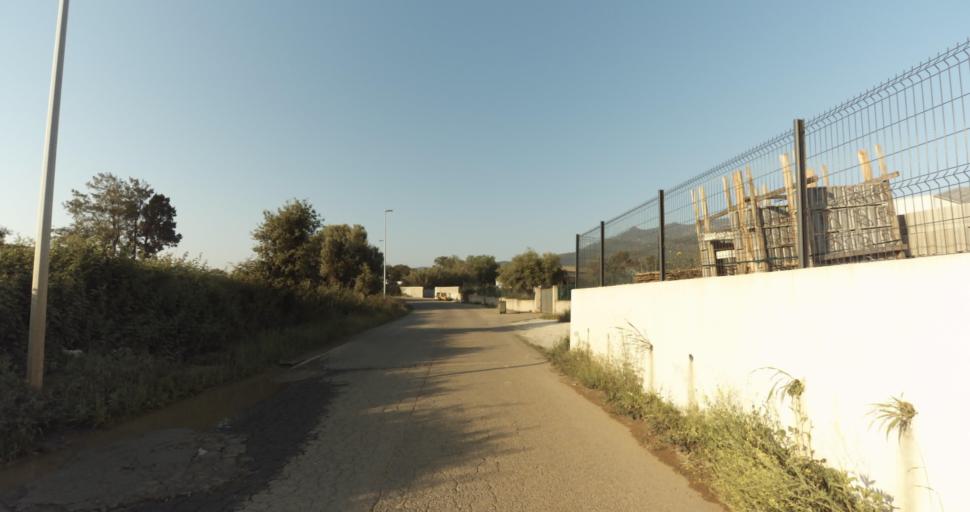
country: FR
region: Corsica
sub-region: Departement de la Haute-Corse
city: Biguglia
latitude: 42.5994
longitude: 9.4417
